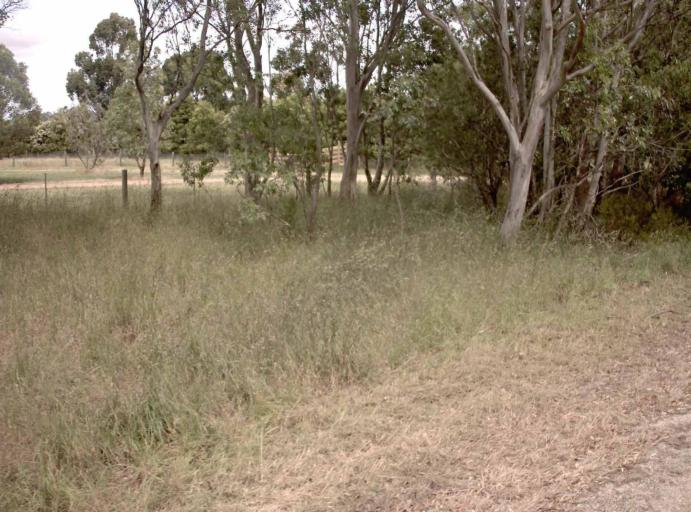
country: AU
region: Victoria
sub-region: Wellington
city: Sale
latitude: -37.9293
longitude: 147.0920
